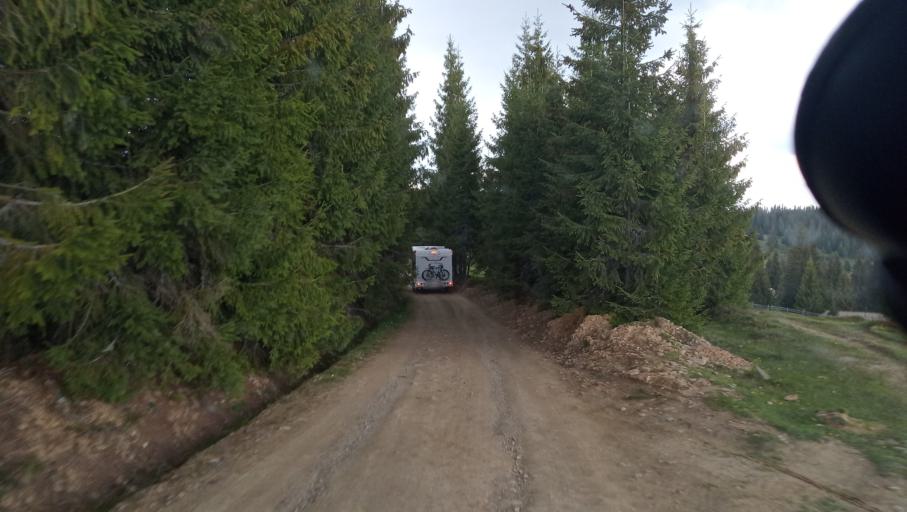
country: RO
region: Cluj
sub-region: Comuna Belis
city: Belis
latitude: 46.6307
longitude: 23.0446
